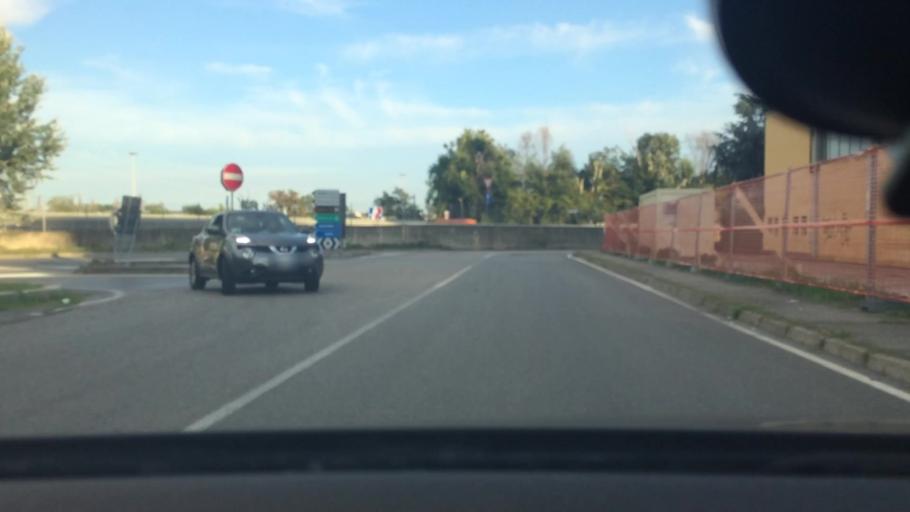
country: IT
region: Lombardy
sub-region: Citta metropolitana di Milano
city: Pero
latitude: 45.5017
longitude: 9.0888
